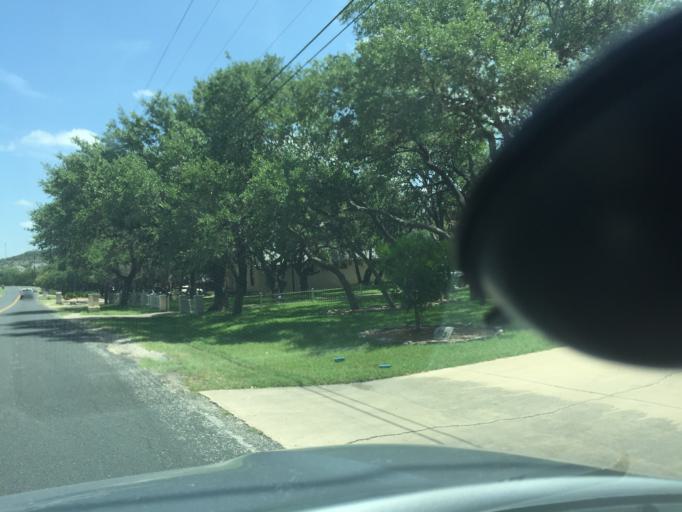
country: US
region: Texas
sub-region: Bexar County
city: Timberwood Park
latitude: 29.6888
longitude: -98.4805
